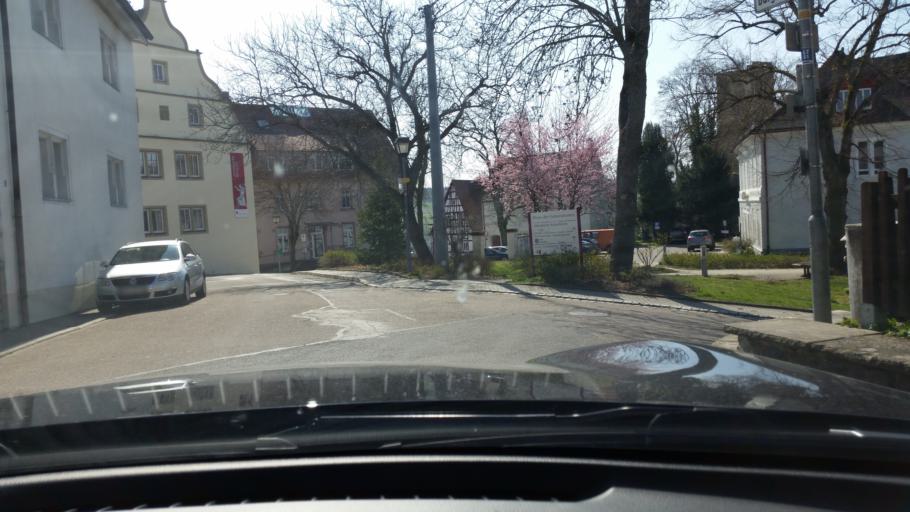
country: DE
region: Baden-Wuerttemberg
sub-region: Regierungsbezirk Stuttgart
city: Krautheim
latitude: 49.3878
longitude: 9.6356
